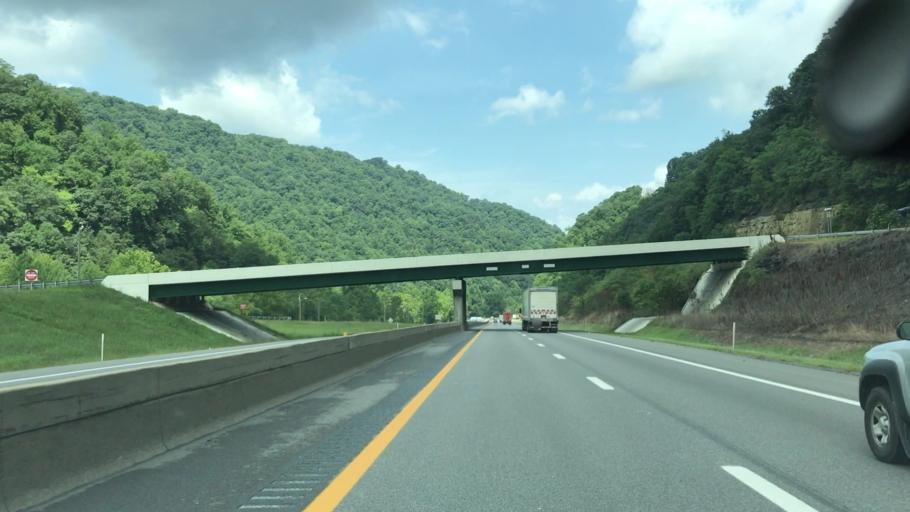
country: US
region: West Virginia
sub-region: Kanawha County
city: Montgomery
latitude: 38.0286
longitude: -81.3568
